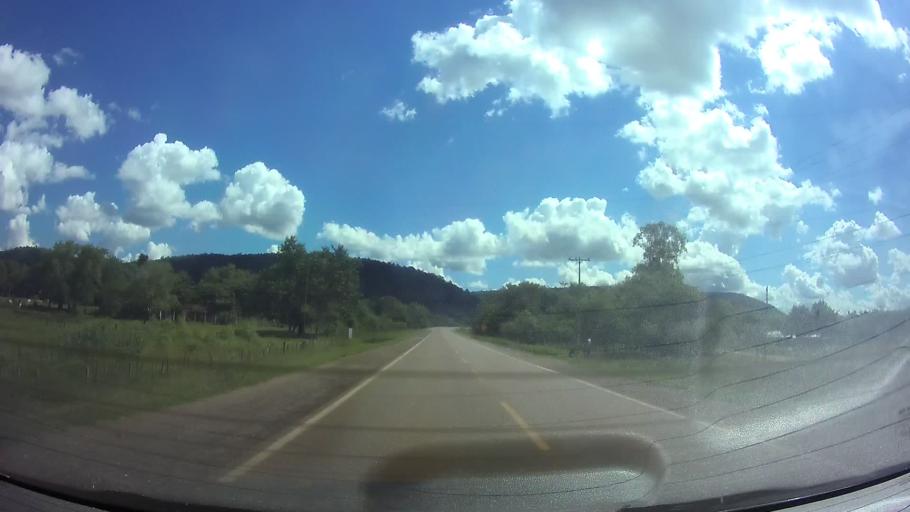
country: PY
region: Paraguari
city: La Colmena
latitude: -25.9160
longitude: -56.7174
